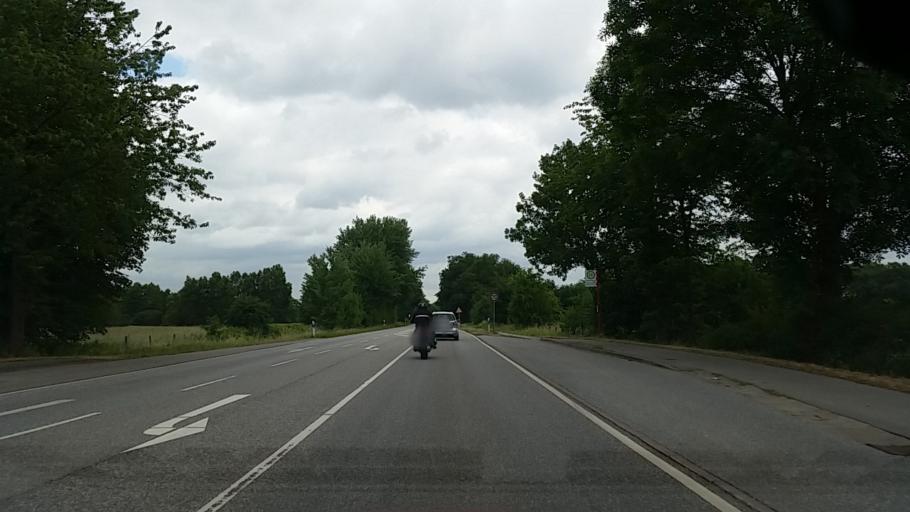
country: DE
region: Schleswig-Holstein
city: Tangstedt
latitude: 53.7141
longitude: 10.0774
